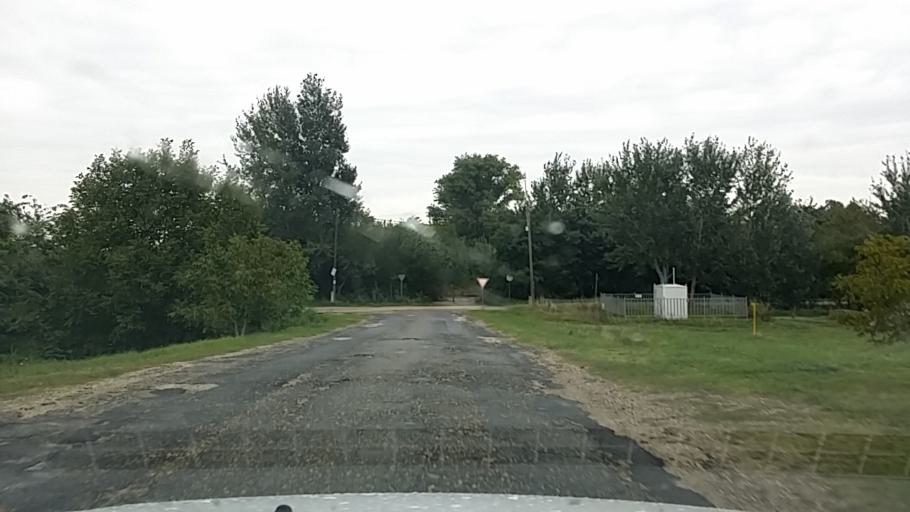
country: HU
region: Pest
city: Domsod
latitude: 47.0779
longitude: 19.0002
